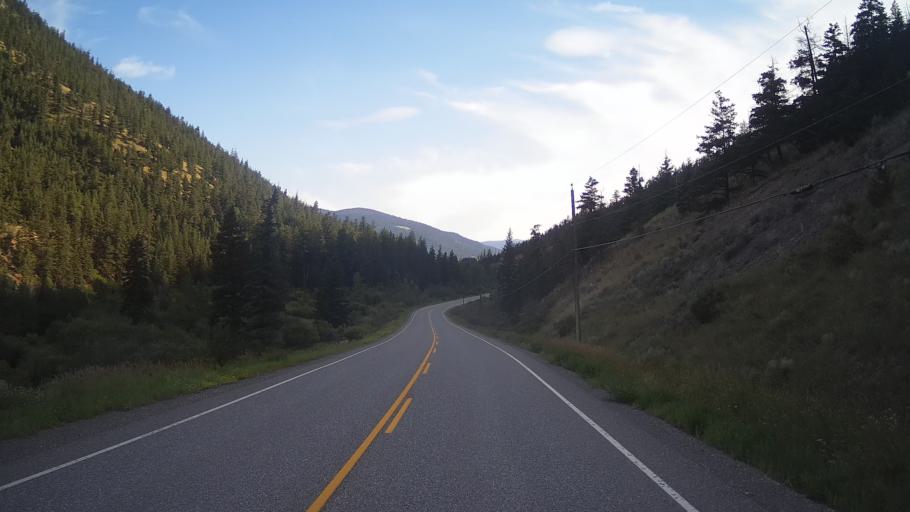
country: CA
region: British Columbia
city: Cache Creek
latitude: 50.8738
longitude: -121.5201
